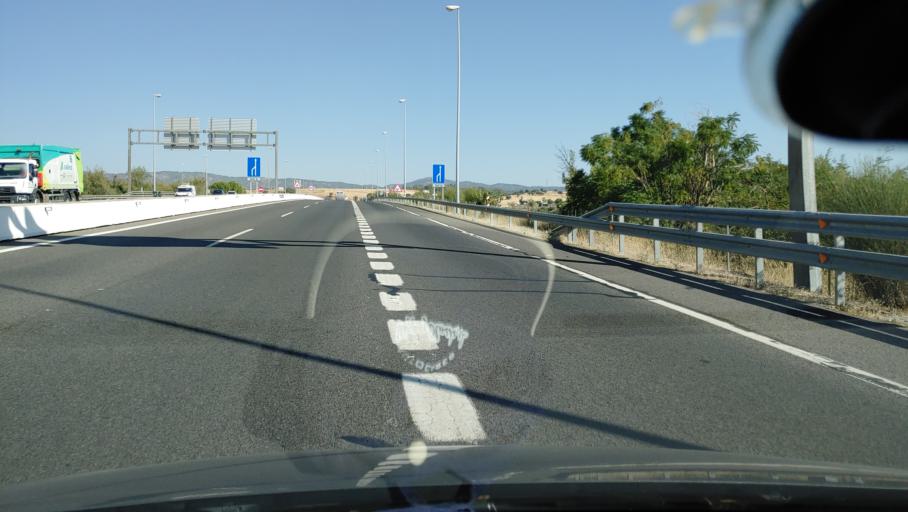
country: ES
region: Andalusia
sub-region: Province of Cordoba
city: Cordoba
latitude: 37.9015
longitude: -4.7496
